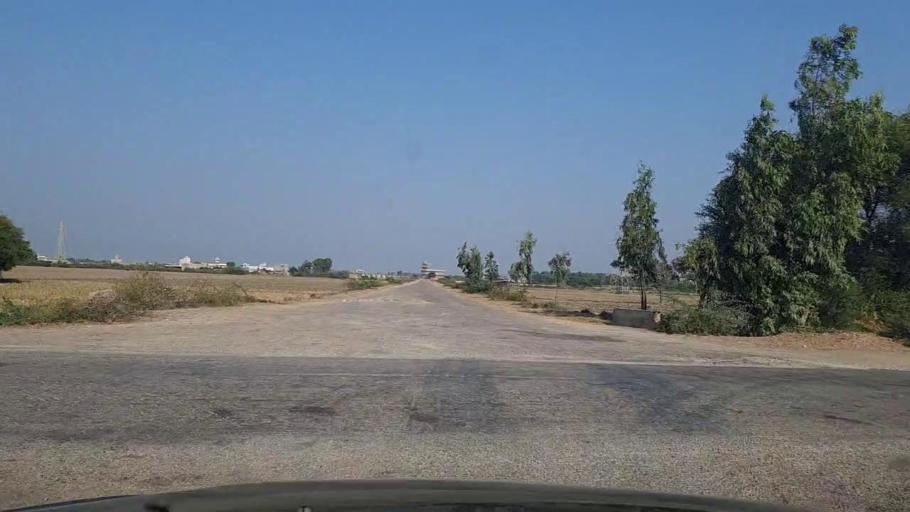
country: PK
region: Sindh
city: Chuhar Jamali
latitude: 24.5893
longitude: 68.0846
